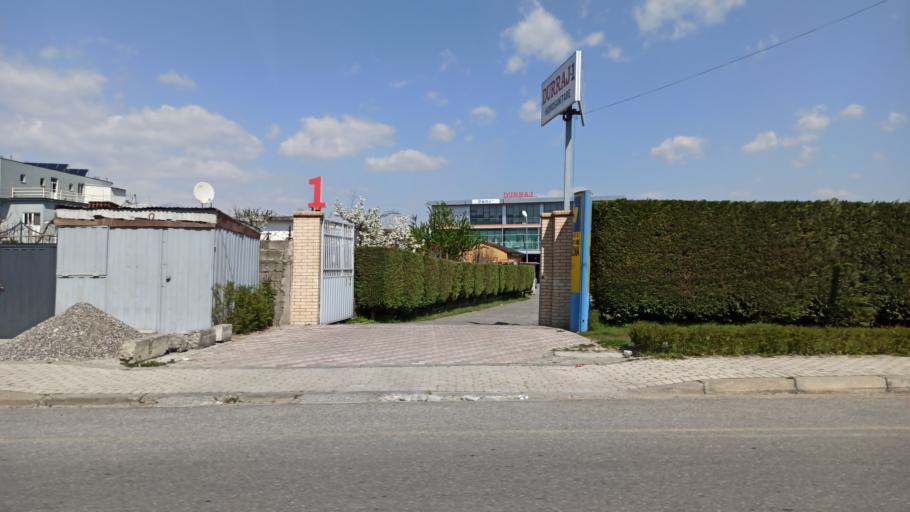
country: AL
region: Shkoder
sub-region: Rrethi i Shkodres
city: Shkoder
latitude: 42.0551
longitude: 19.5179
